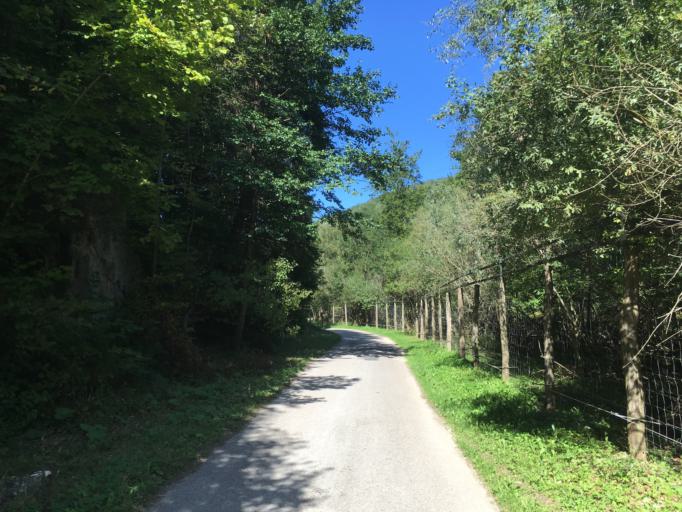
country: SK
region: Trenciansky
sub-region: Okres Povazska Bystrica
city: Povazska Bystrica
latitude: 49.0228
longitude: 18.4388
